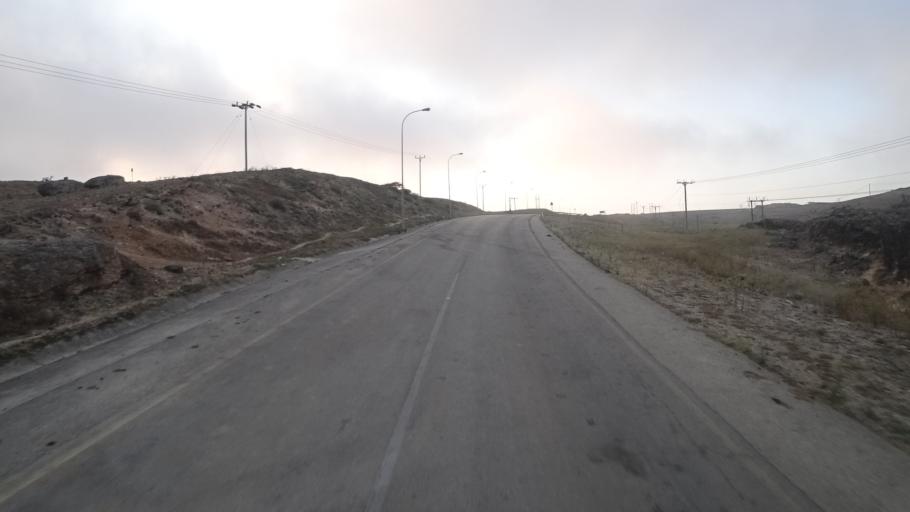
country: OM
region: Zufar
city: Salalah
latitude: 17.1209
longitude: 53.9304
